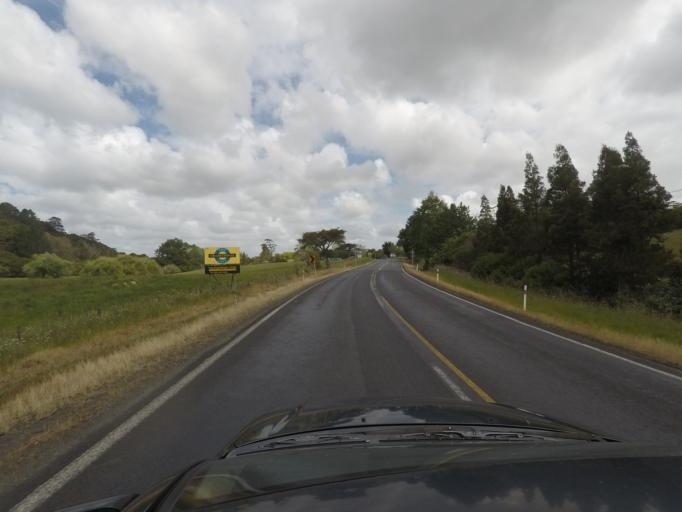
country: NZ
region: Auckland
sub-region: Auckland
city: Parakai
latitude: -36.6057
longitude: 174.4891
